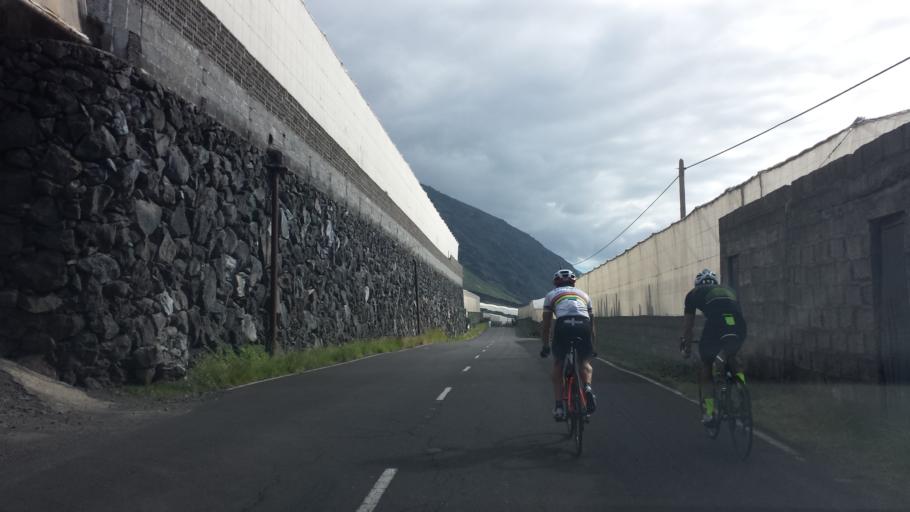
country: ES
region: Canary Islands
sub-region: Provincia de Santa Cruz de Tenerife
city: Fuencaliente de la Palma
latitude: 28.5635
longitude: -17.8913
